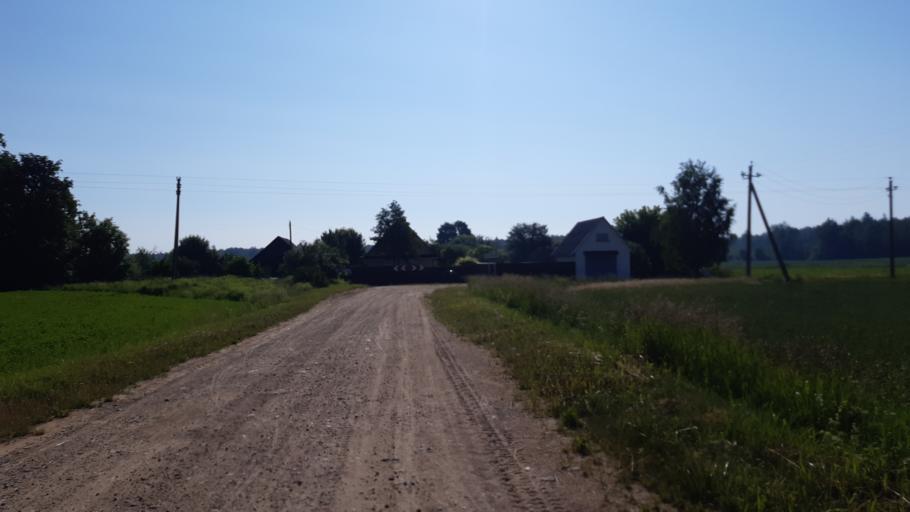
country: BY
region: Minsk
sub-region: Smalyavitski Rayon
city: Oktjabr'skij
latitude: 54.0952
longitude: 28.1999
